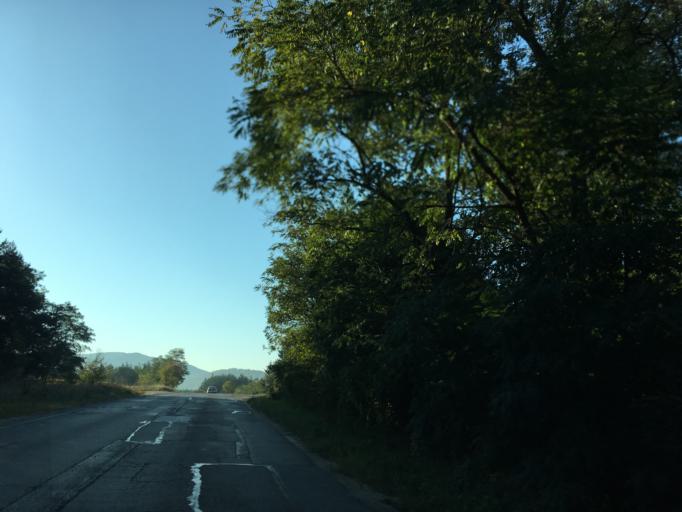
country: BG
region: Sofiya
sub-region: Obshtina Ikhtiman
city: Ikhtiman
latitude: 42.3762
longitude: 23.8772
